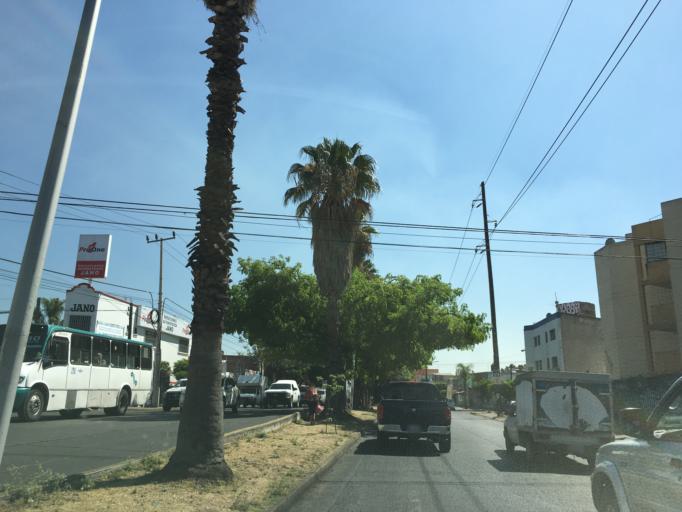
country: MX
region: Jalisco
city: Guadalajara
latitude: 20.6393
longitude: -103.3920
